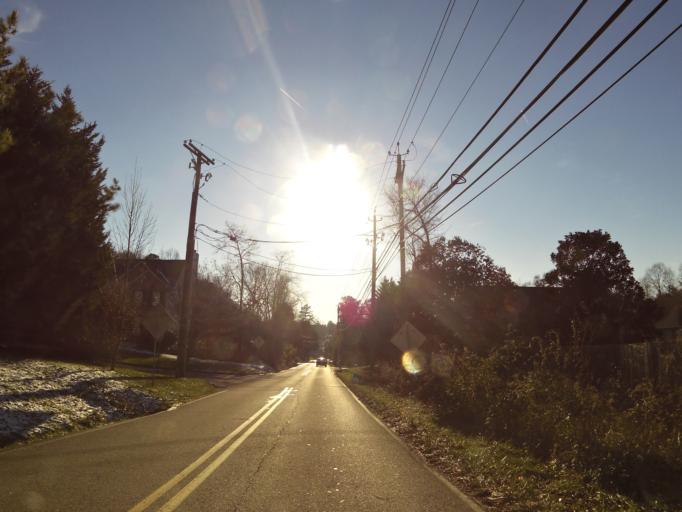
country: US
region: Tennessee
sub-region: Knox County
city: Farragut
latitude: 35.9589
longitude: -84.0673
